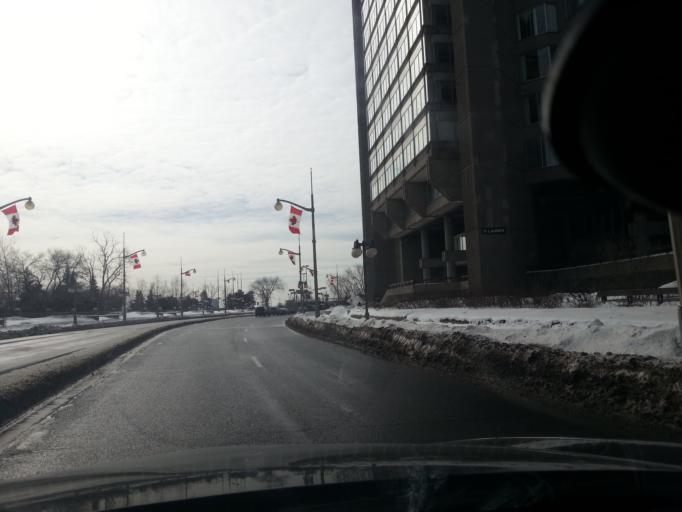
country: CA
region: Ontario
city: Ottawa
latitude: 45.4255
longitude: -75.7121
